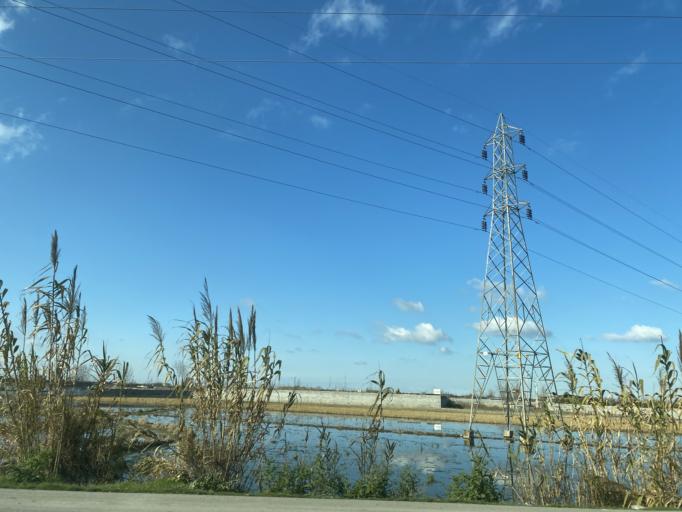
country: IR
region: Mazandaran
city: Babol
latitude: 36.5249
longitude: 52.6128
